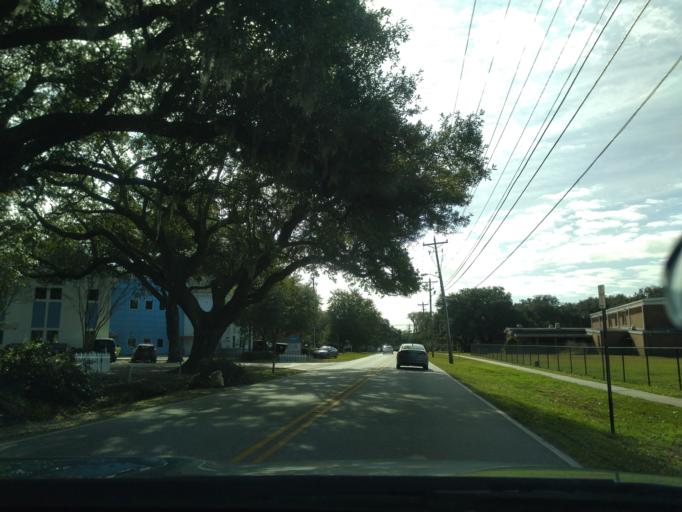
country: US
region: South Carolina
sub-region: Charleston County
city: North Charleston
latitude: 32.7923
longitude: -80.0187
